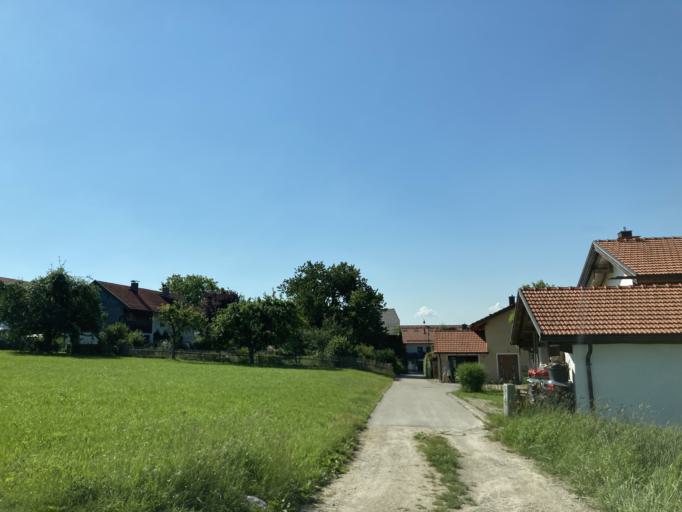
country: DE
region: Bavaria
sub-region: Upper Bavaria
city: Hoslwang
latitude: 47.9534
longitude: 12.3093
